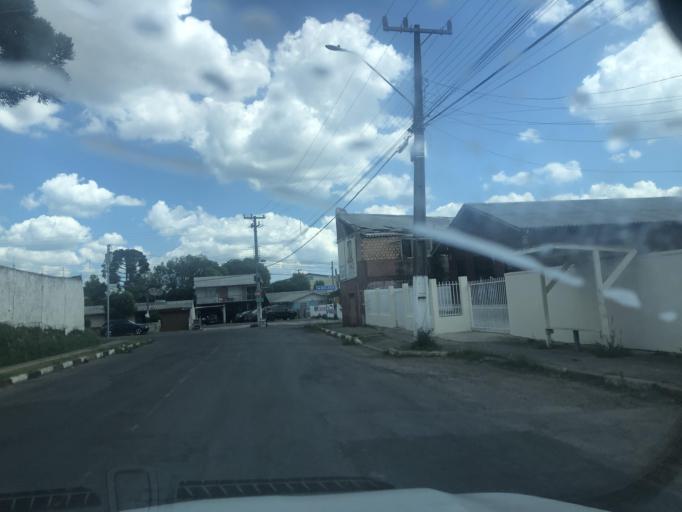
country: BR
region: Santa Catarina
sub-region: Lages
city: Lages
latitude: -27.7957
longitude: -50.3136
